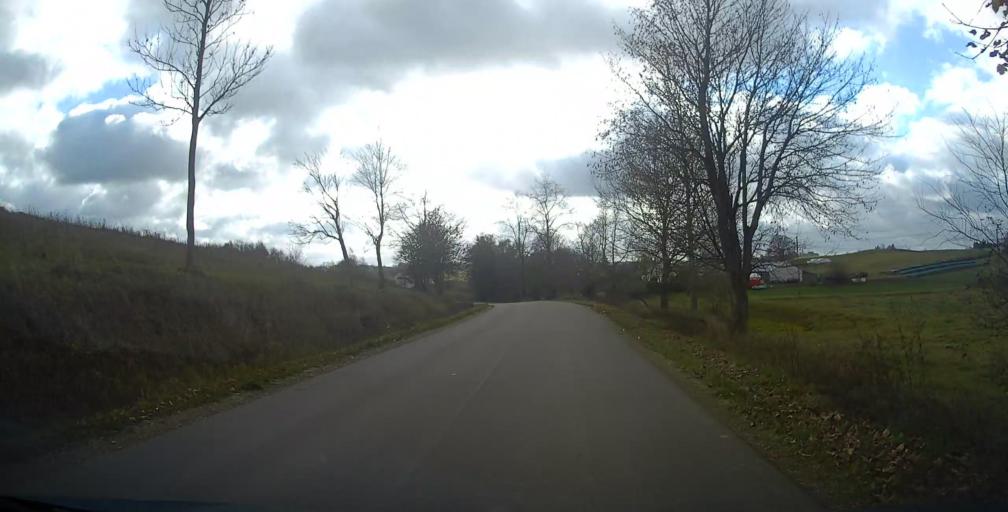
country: PL
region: Podlasie
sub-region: Suwalki
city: Suwalki
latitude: 54.3333
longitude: 22.8589
